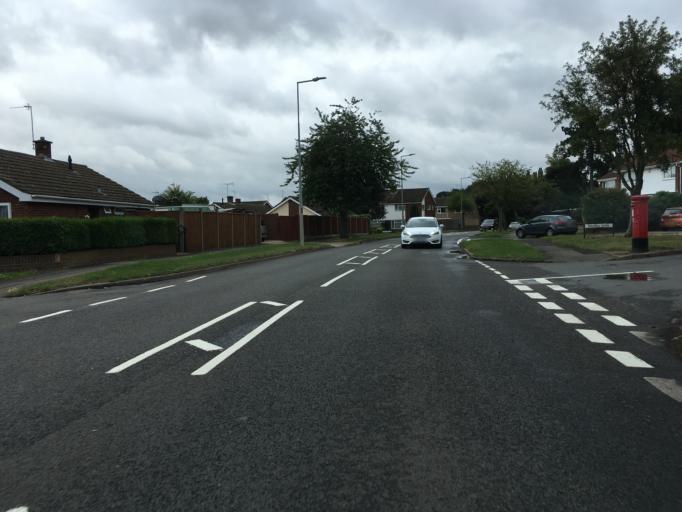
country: GB
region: England
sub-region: Buckinghamshire
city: Bletchley
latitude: 52.0048
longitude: -0.7416
